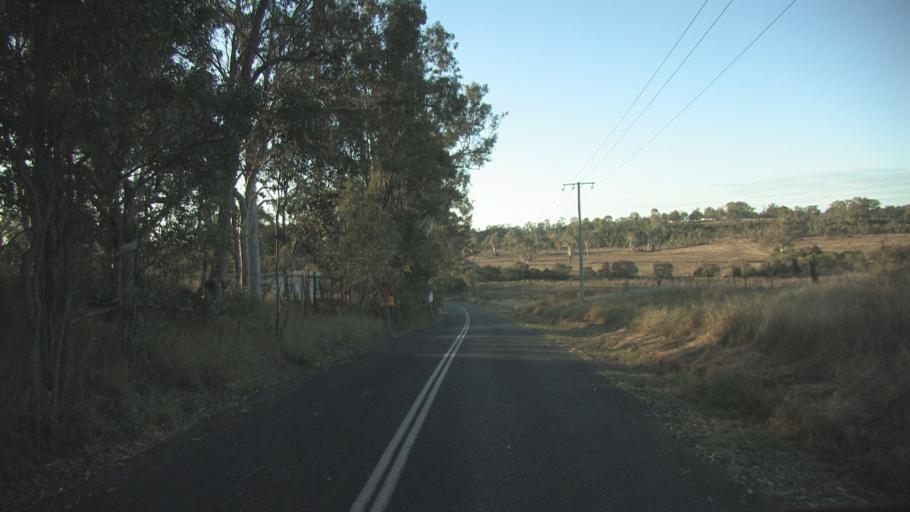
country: AU
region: Queensland
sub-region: Logan
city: Cedar Vale
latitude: -27.8612
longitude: 153.1225
